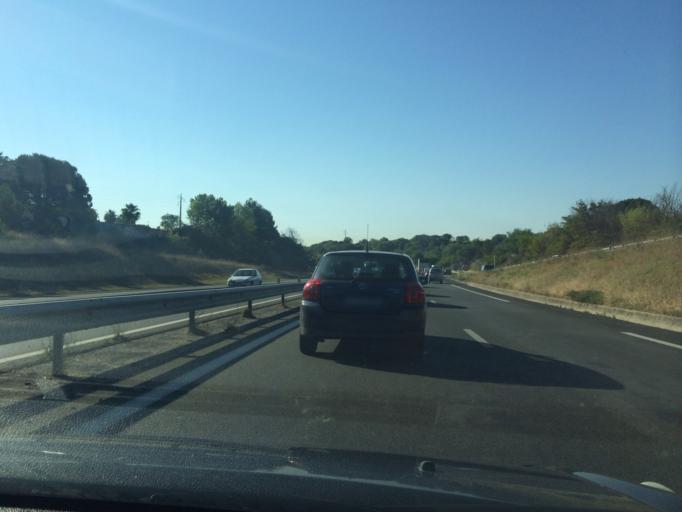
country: FR
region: Languedoc-Roussillon
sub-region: Departement de l'Herault
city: Juvignac
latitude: 43.6103
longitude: 3.8028
